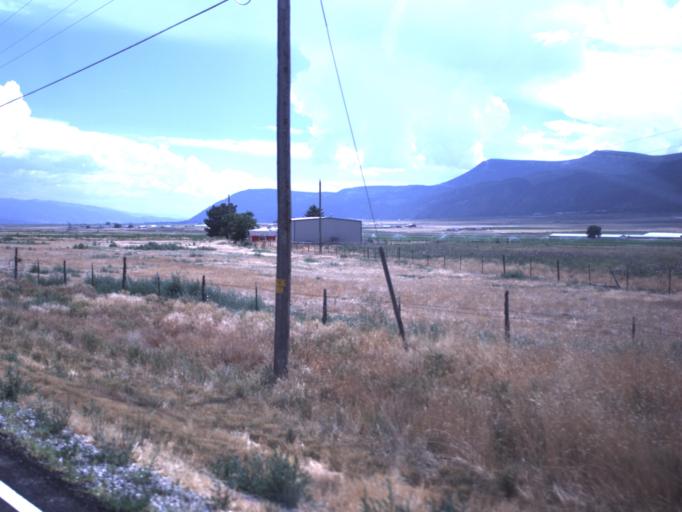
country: US
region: Utah
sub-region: Sanpete County
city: Fountain Green
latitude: 39.5960
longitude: -111.6196
